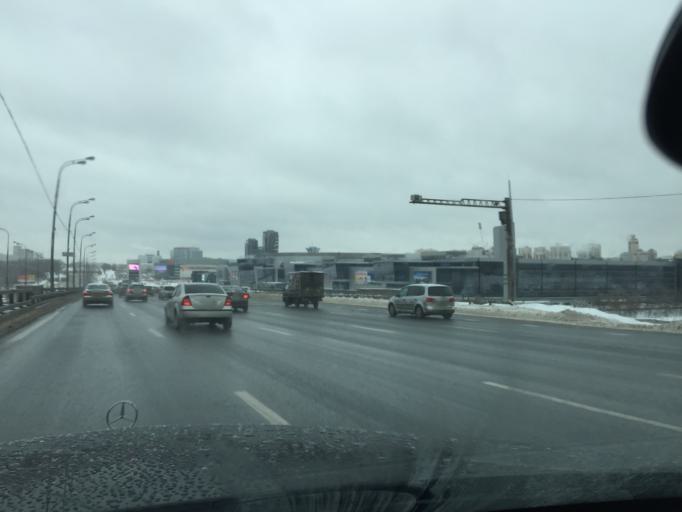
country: RU
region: Moscow
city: Strogino
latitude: 55.8307
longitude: 37.3948
